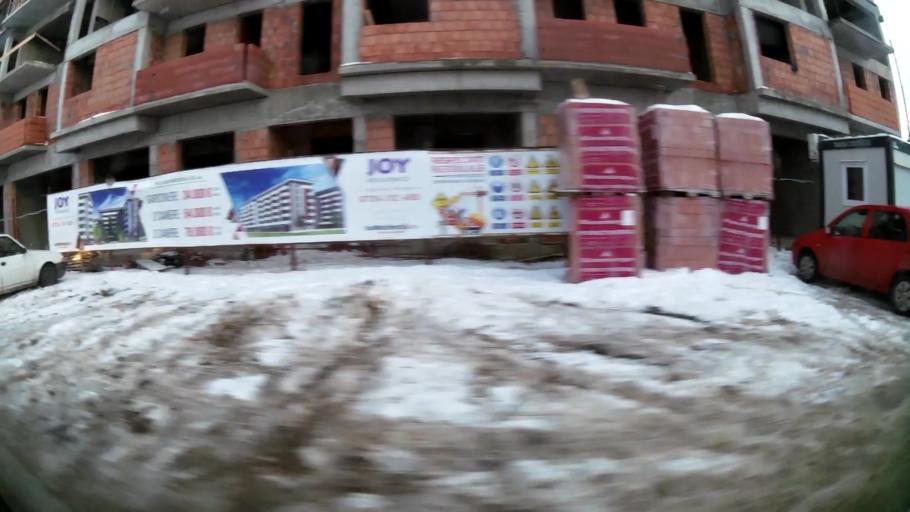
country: RO
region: Ilfov
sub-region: Comuna Popesti-Leordeni
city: Popesti-Leordeni
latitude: 44.3675
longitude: 26.1546
